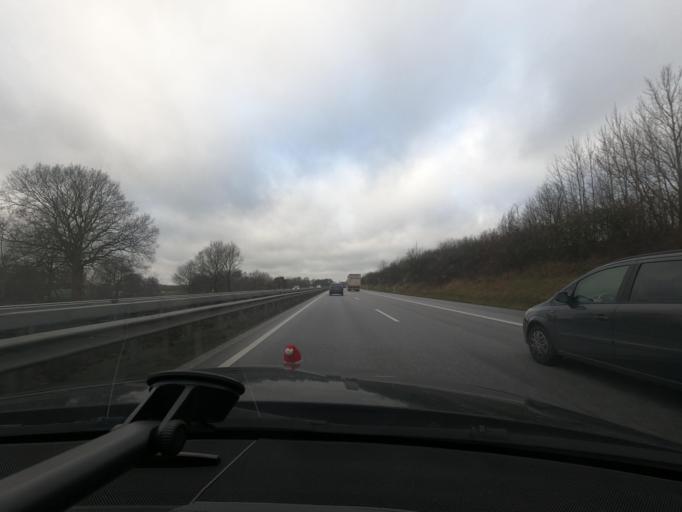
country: DE
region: Schleswig-Holstein
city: Bokel
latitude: 54.2386
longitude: 9.8236
